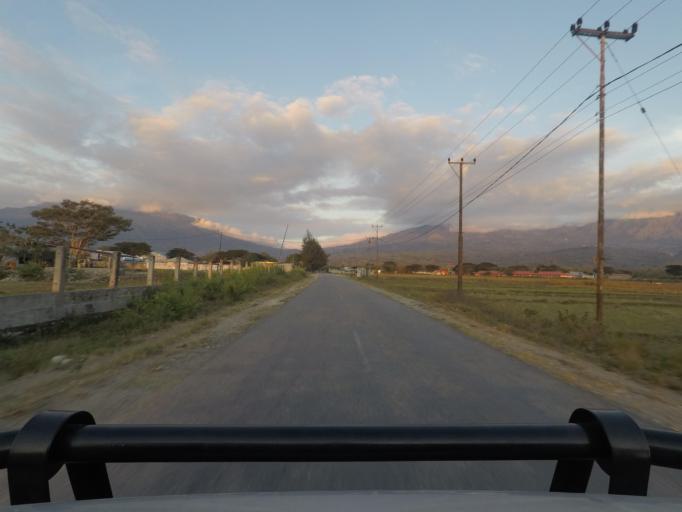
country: TL
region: Bobonaro
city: Maliana
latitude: -8.9919
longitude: 125.1874
